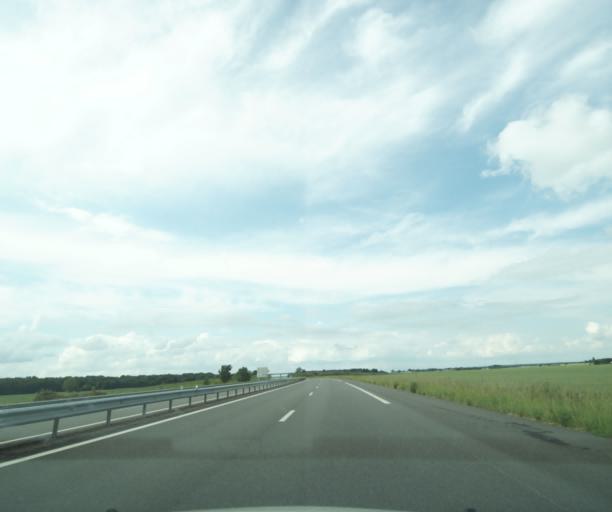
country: FR
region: Centre
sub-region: Departement du Cher
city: Levet
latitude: 46.9269
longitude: 2.4263
